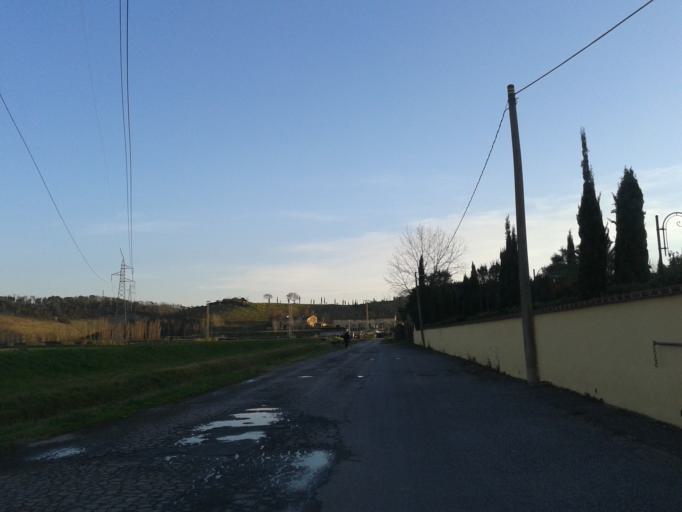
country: IT
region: Tuscany
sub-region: Provincia di Livorno
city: Guasticce
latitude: 43.5950
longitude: 10.4054
